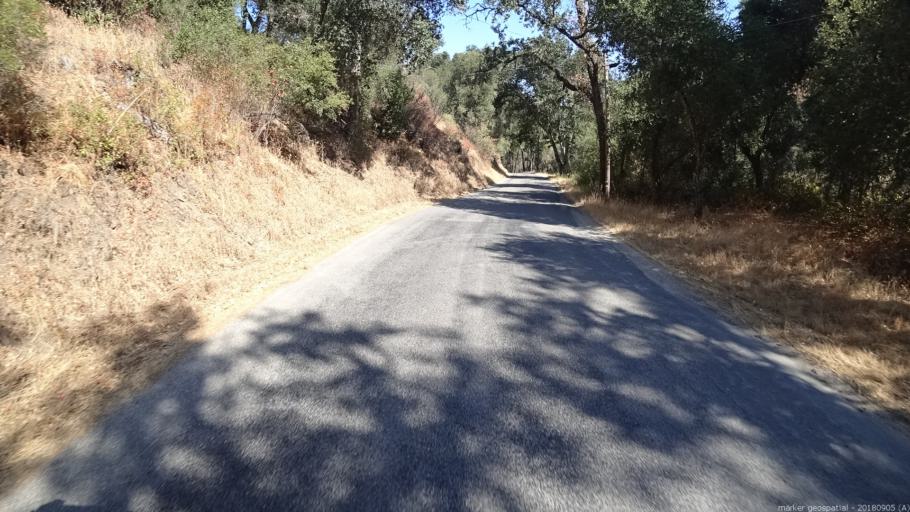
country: US
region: California
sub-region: Monterey County
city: Gonzales
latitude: 36.3815
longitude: -121.5934
